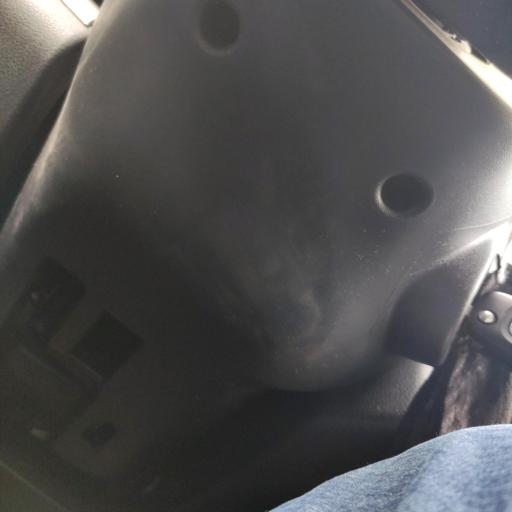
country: RU
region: Samara
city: Smyshlyayevka
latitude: 53.2153
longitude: 50.3343
